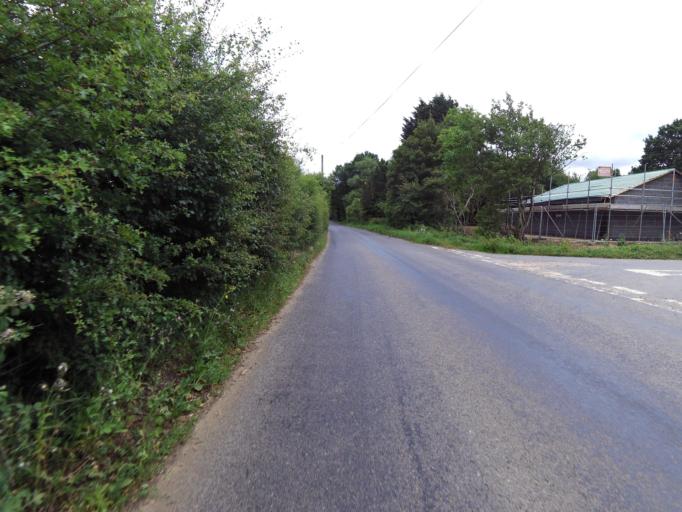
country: GB
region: England
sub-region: Norfolk
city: Harleston
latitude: 52.3978
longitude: 1.2193
